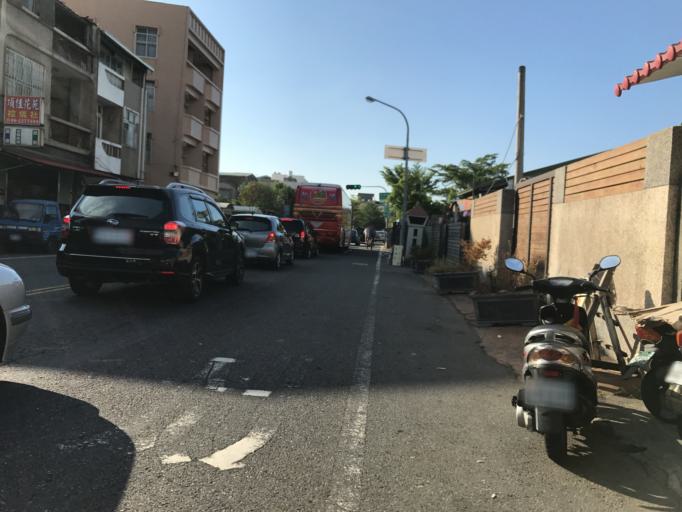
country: TW
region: Taiwan
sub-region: Tainan
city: Tainan
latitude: 23.0023
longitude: 120.1647
